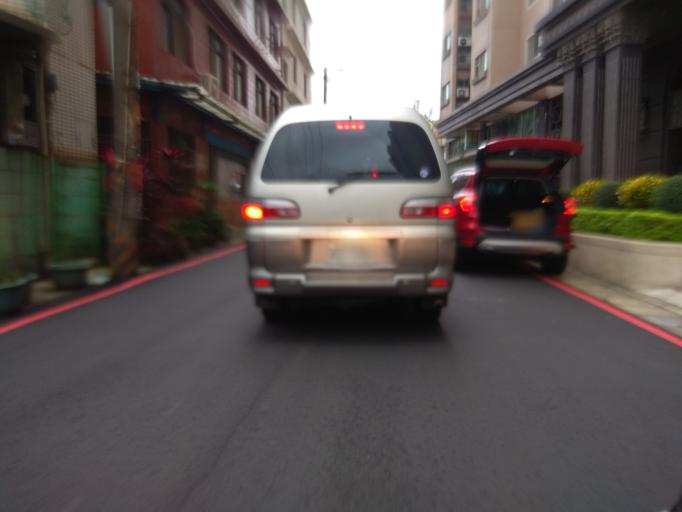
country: TW
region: Taiwan
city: Daxi
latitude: 24.9427
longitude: 121.2060
